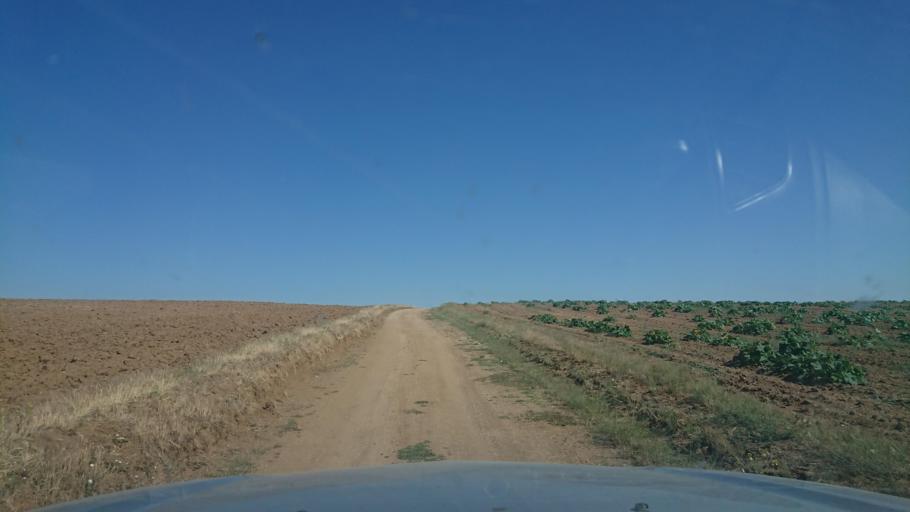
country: TR
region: Aksaray
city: Agacoren
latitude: 38.8475
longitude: 33.9174
